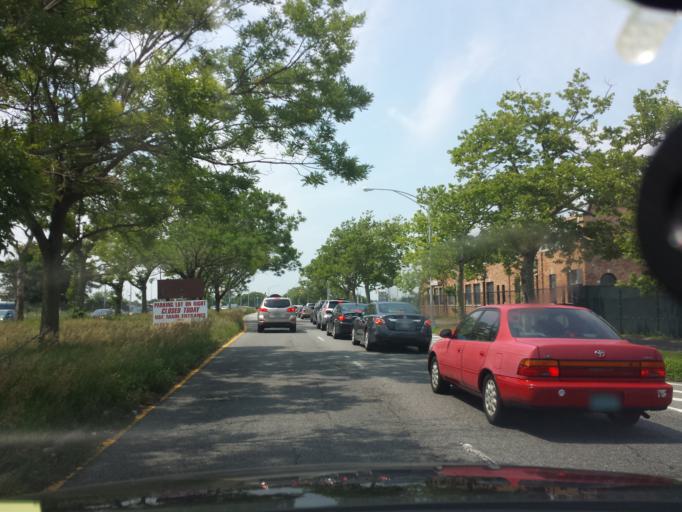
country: US
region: New York
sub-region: Kings County
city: Brooklyn
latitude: 40.5891
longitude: -73.8997
